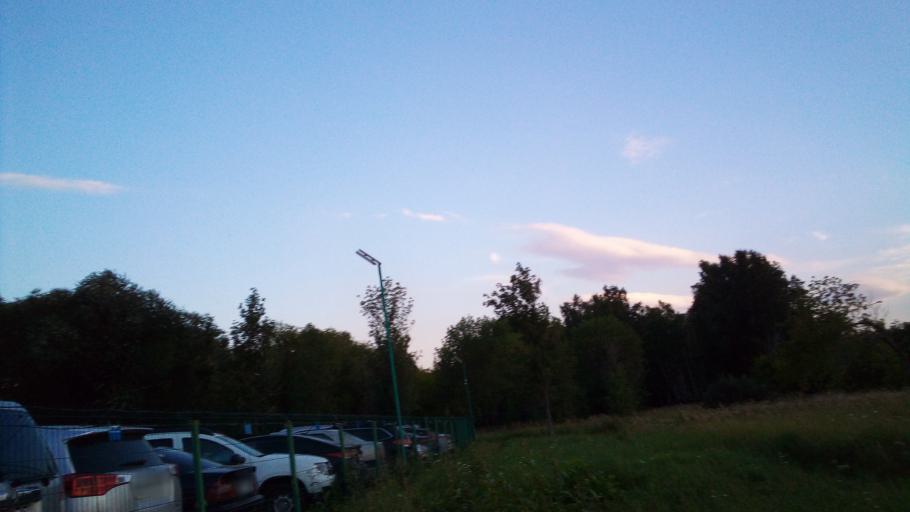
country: RU
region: Chelyabinsk
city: Potanino
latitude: 55.2904
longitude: 61.5114
